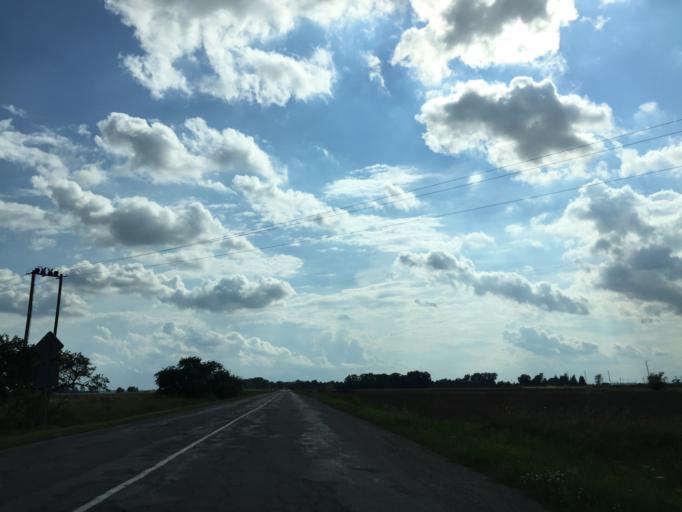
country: LV
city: Tervete
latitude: 56.5965
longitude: 23.4844
